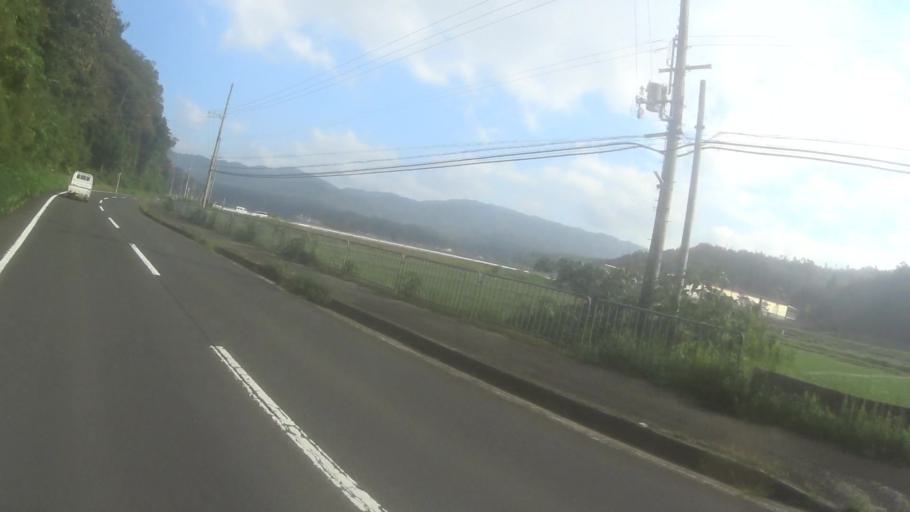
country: JP
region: Kyoto
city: Miyazu
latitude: 35.5871
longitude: 135.1319
